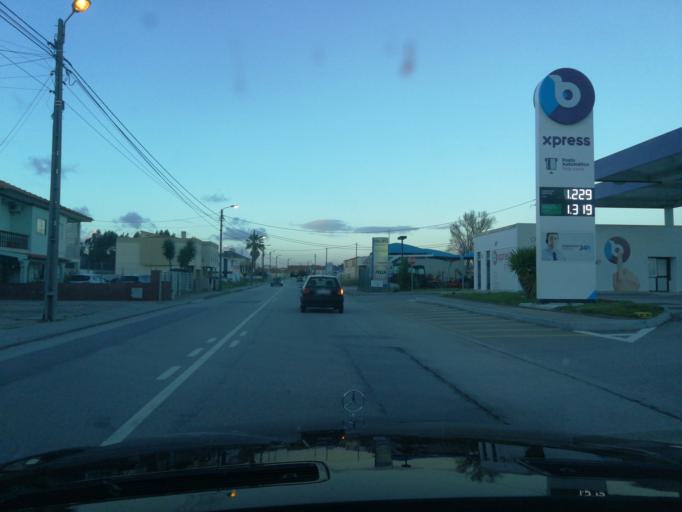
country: PT
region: Aveiro
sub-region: Estarreja
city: Estarreja
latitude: 40.7645
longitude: -8.5714
